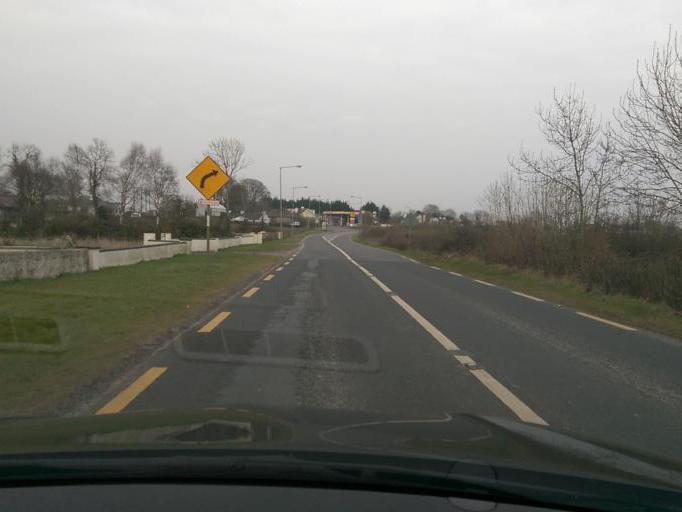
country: IE
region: Leinster
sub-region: An Longfort
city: Lanesborough
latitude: 53.6762
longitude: -8.0185
